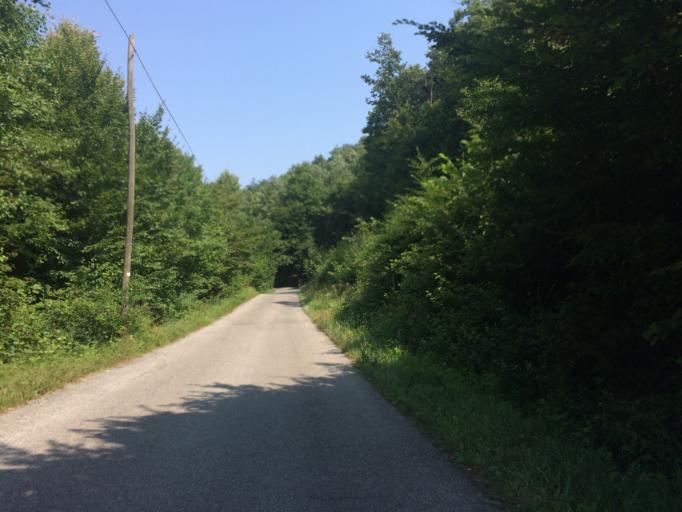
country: IT
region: Liguria
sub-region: Provincia di Savona
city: Molino-Pera
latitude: 44.4830
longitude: 8.3525
